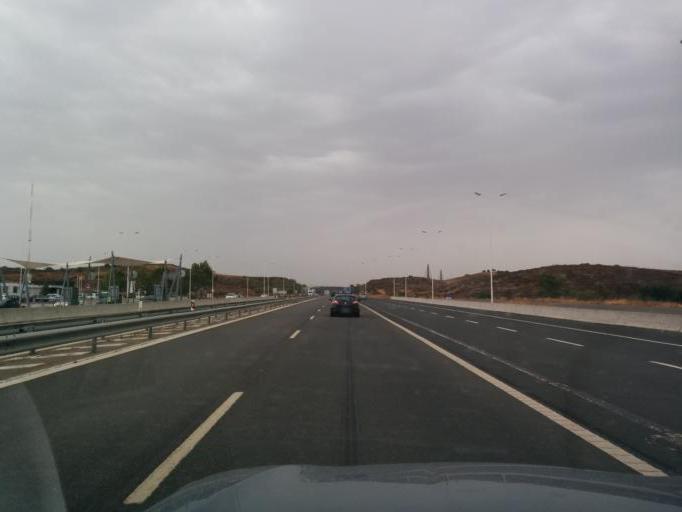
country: PT
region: Faro
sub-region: Castro Marim
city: Castro Marim
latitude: 37.2361
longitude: -7.4391
